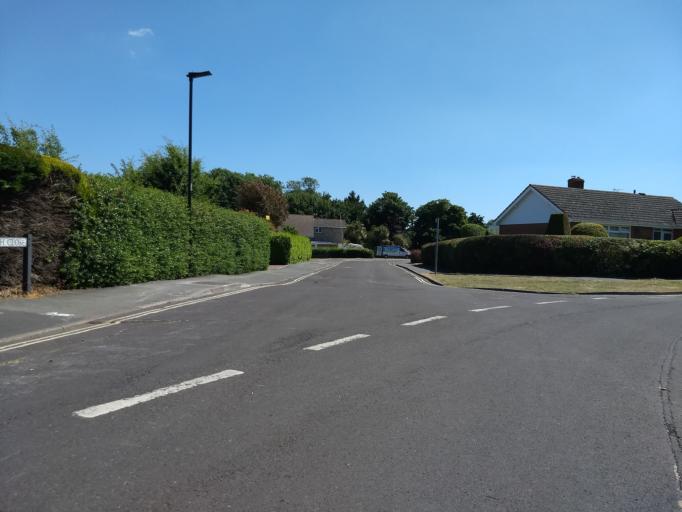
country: GB
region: England
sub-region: Isle of Wight
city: Cowes
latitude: 50.7618
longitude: -1.3061
